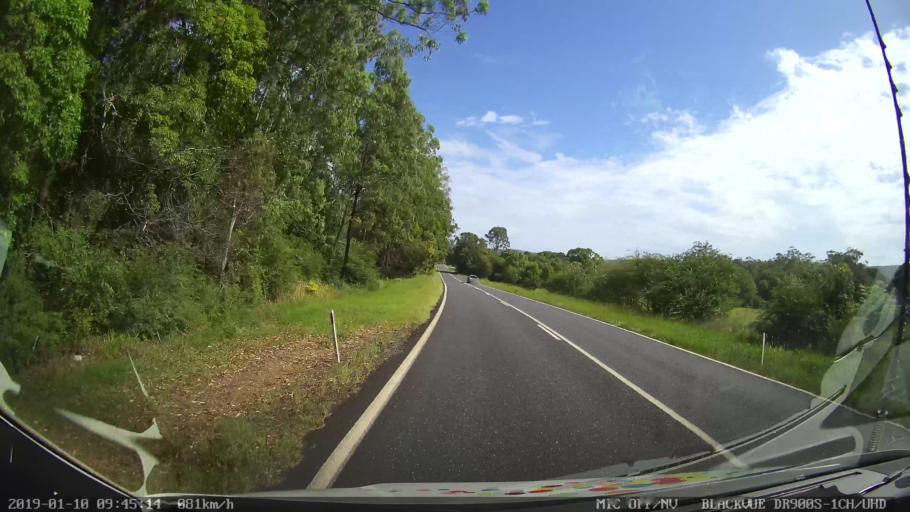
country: AU
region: New South Wales
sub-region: Coffs Harbour
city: Nana Glen
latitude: -30.1072
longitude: 153.0041
